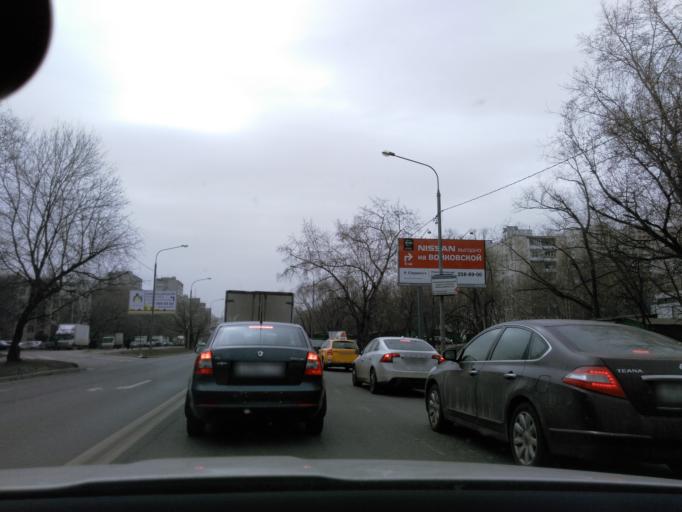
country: RU
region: Moscow
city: Novokhovrino
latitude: 55.8614
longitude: 37.5062
